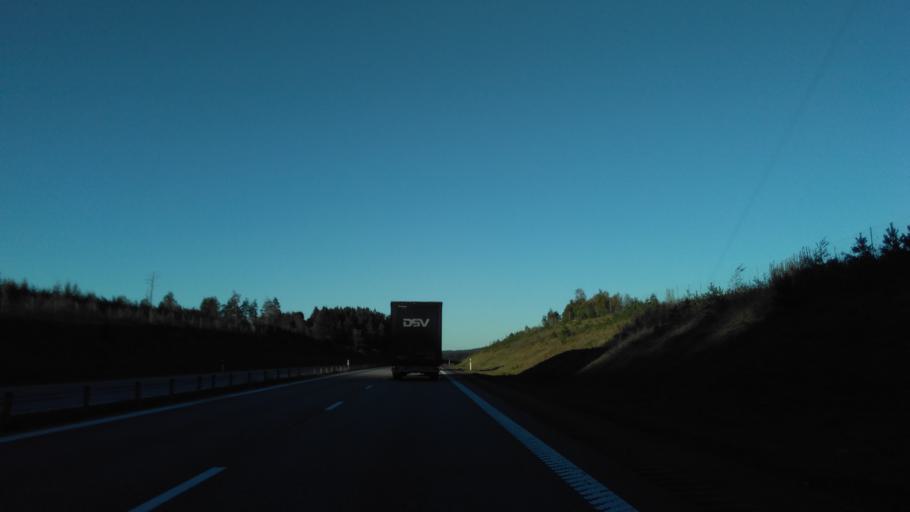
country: SE
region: Vaestra Goetaland
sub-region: Boras Kommun
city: Dalsjofors
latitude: 57.7762
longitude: 13.1166
